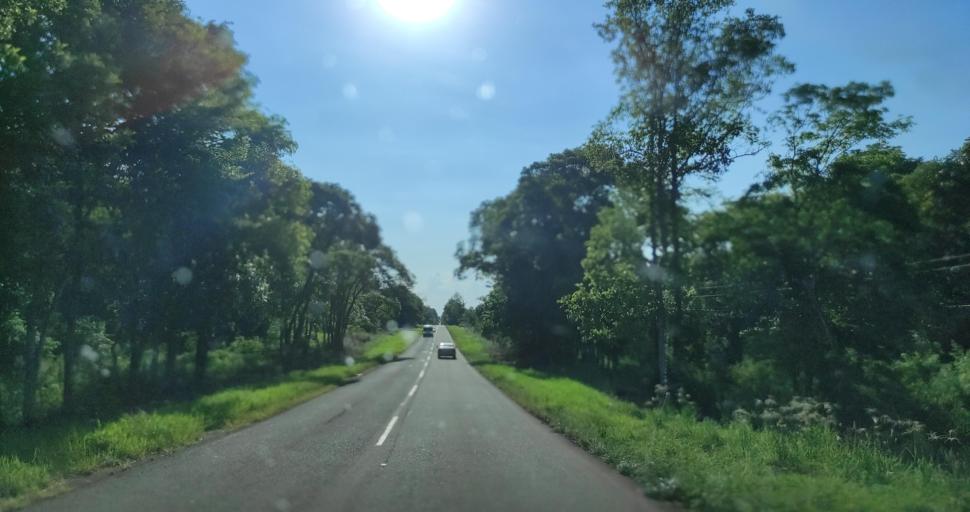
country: AR
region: Misiones
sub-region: Departamento de Eldorado
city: Eldorado
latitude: -26.3996
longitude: -54.3824
